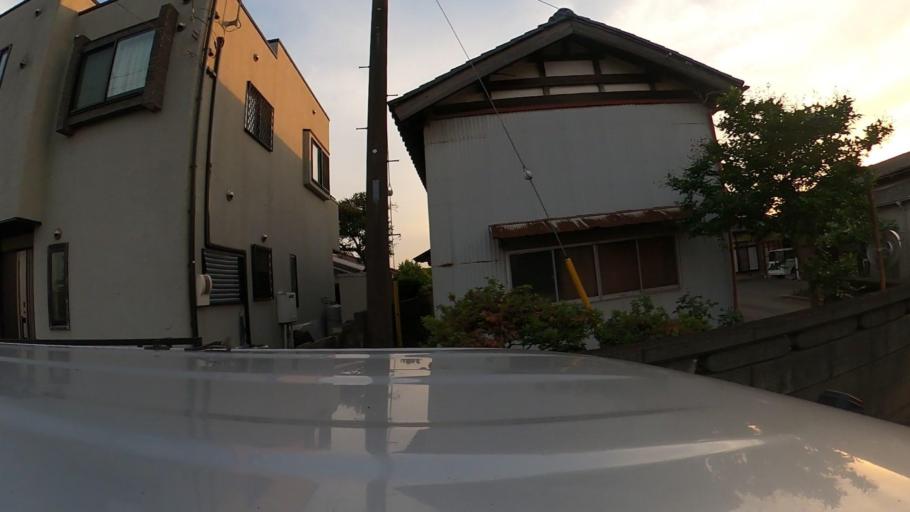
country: JP
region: Ibaraki
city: Ushiku
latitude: 36.0234
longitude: 140.0947
